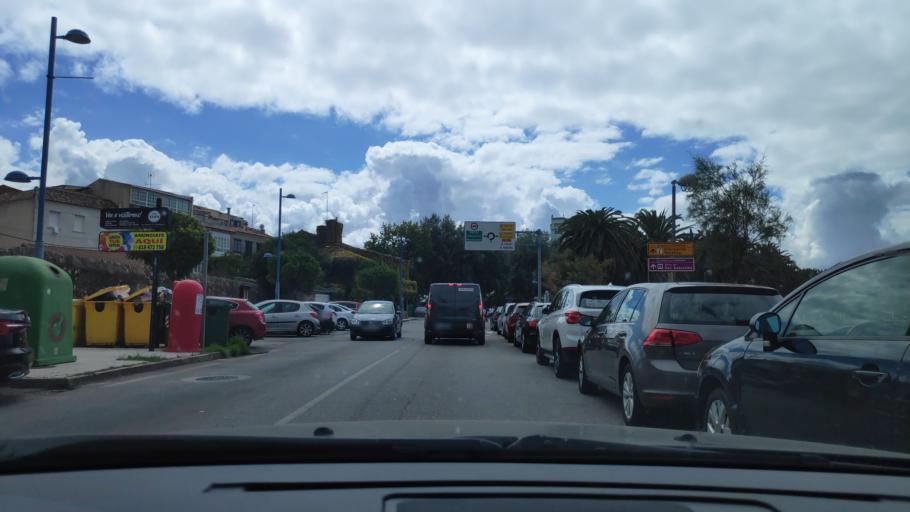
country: ES
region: Galicia
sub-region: Provincia de Pontevedra
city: Cambados
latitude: 42.5174
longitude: -8.8156
